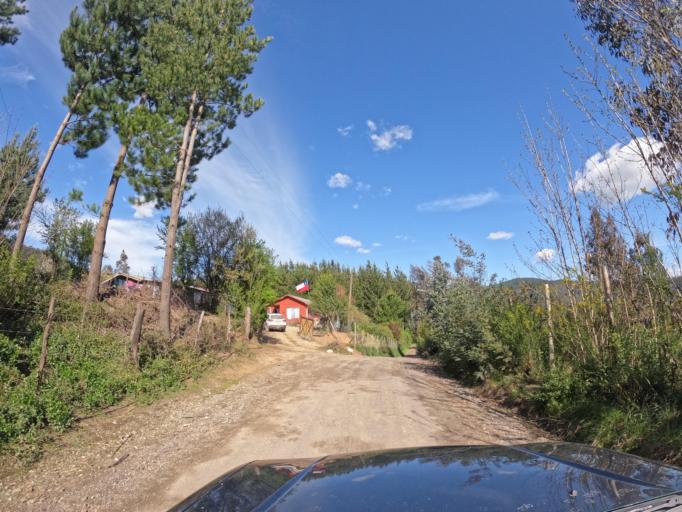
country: CL
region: Biobio
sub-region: Provincia de Concepcion
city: Chiguayante
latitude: -37.0620
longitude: -72.8896
